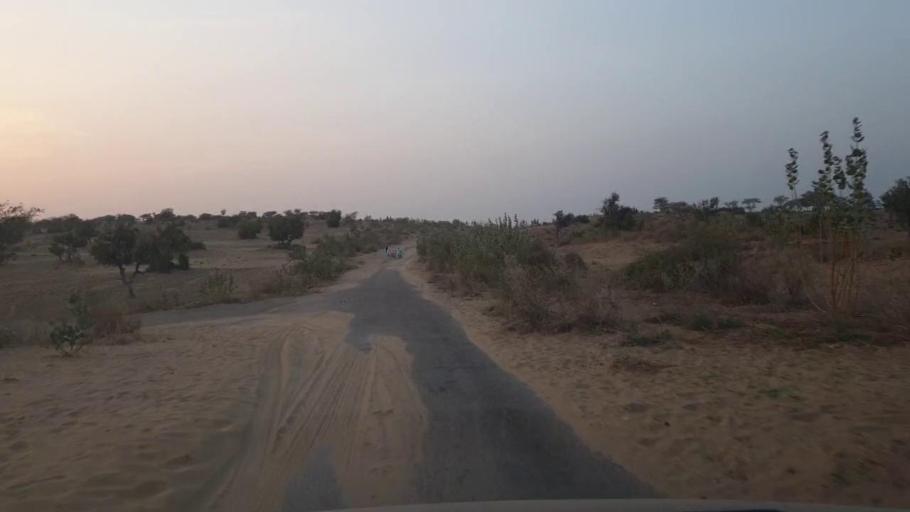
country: PK
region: Sindh
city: Umarkot
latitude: 25.3402
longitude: 70.0528
